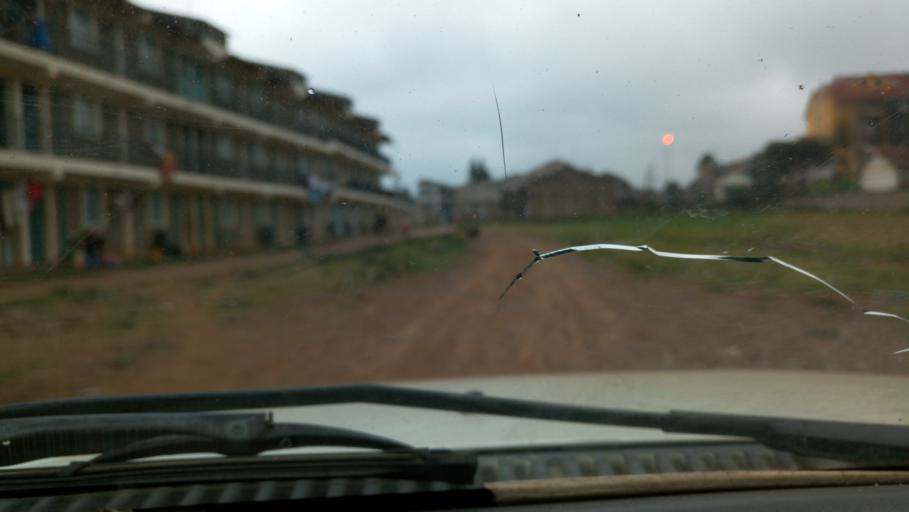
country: KE
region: Nairobi Area
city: Nairobi
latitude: -1.3065
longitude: 36.7755
